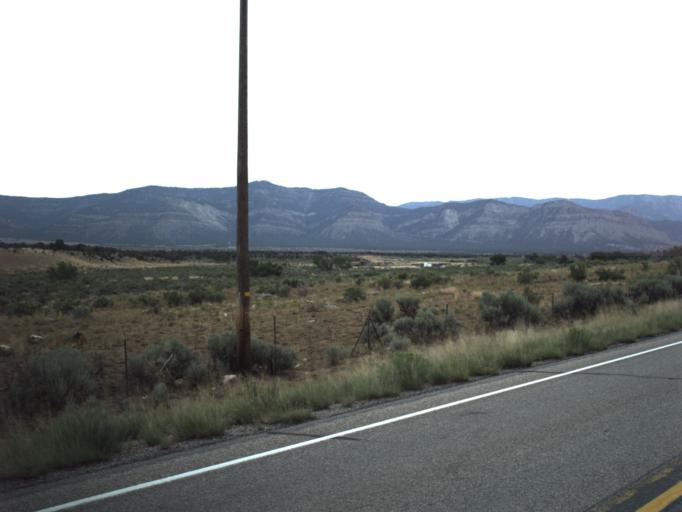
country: US
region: Utah
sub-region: Carbon County
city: East Carbon City
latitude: 39.5355
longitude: -110.4724
